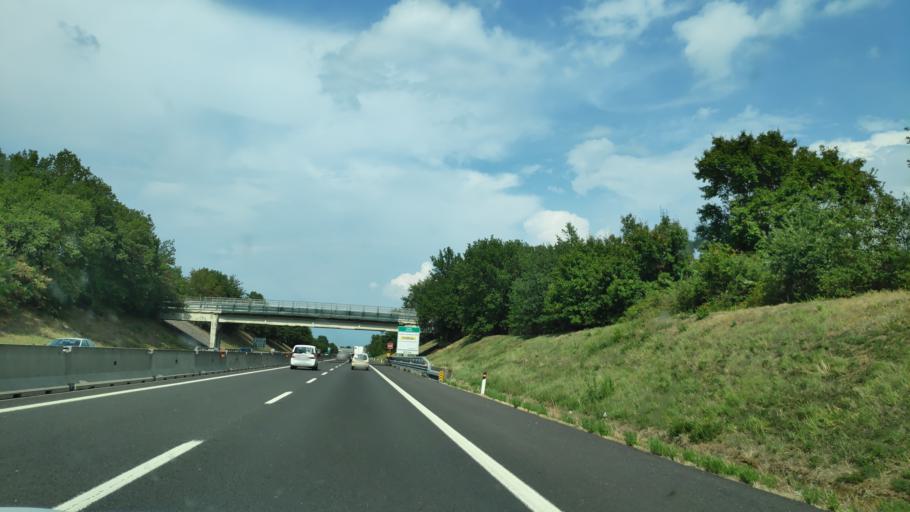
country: IT
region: Tuscany
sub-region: Province of Arezzo
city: Badia al Pino
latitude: 43.4171
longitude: 11.7706
